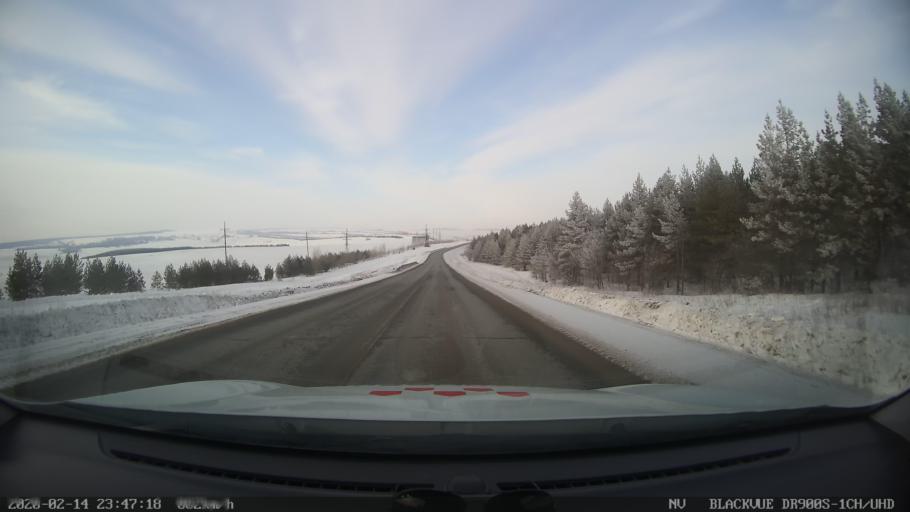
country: RU
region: Tatarstan
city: Kuybyshevskiy Zaton
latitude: 55.2371
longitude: 49.2101
